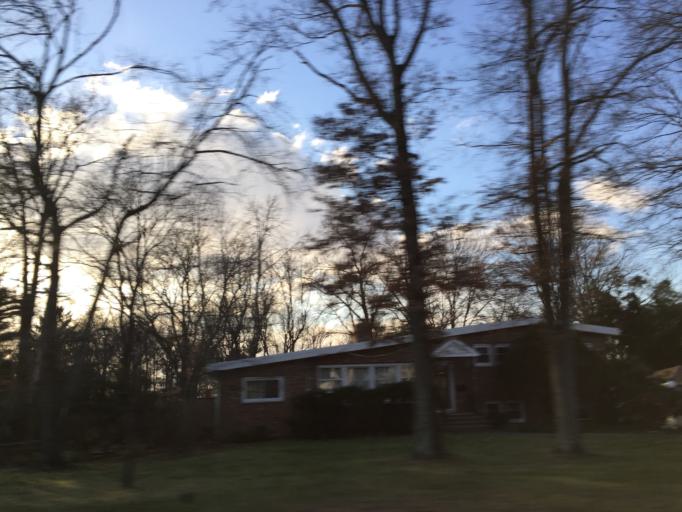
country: US
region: New Jersey
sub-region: Union County
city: Summit
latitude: 40.7277
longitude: -74.3679
